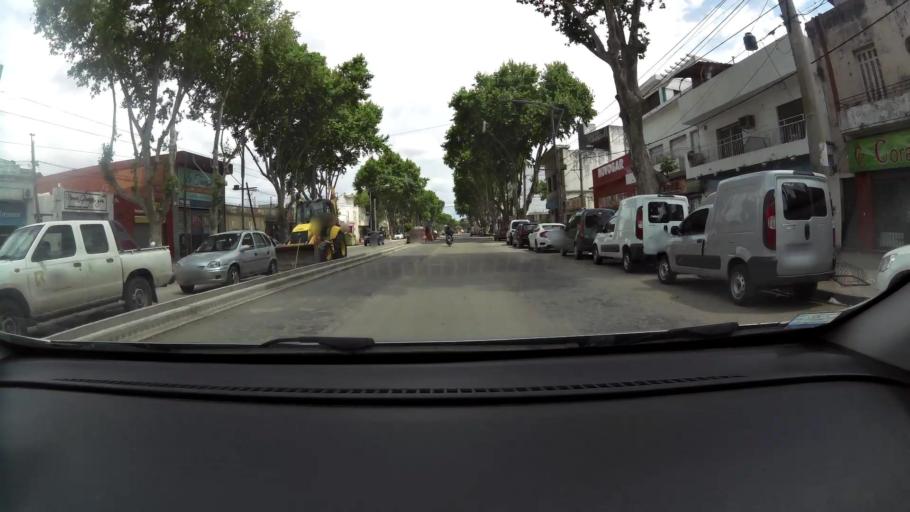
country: AR
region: Santa Fe
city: Gobernador Galvez
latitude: -33.0004
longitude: -60.6488
